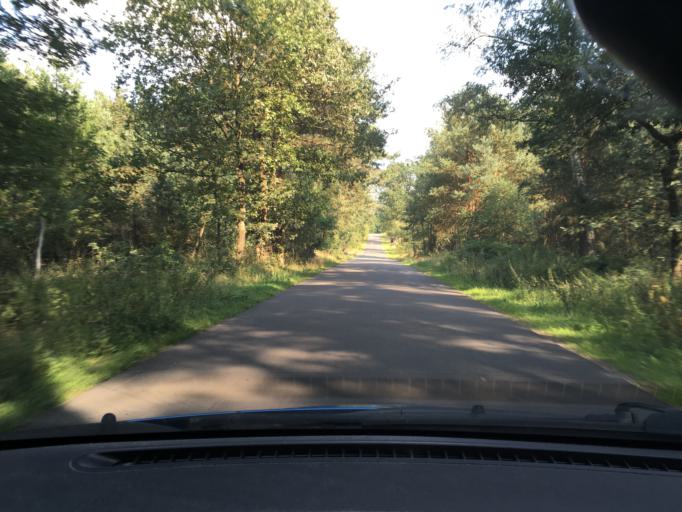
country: DE
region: Lower Saxony
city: Soderstorf
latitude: 53.1432
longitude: 10.1818
